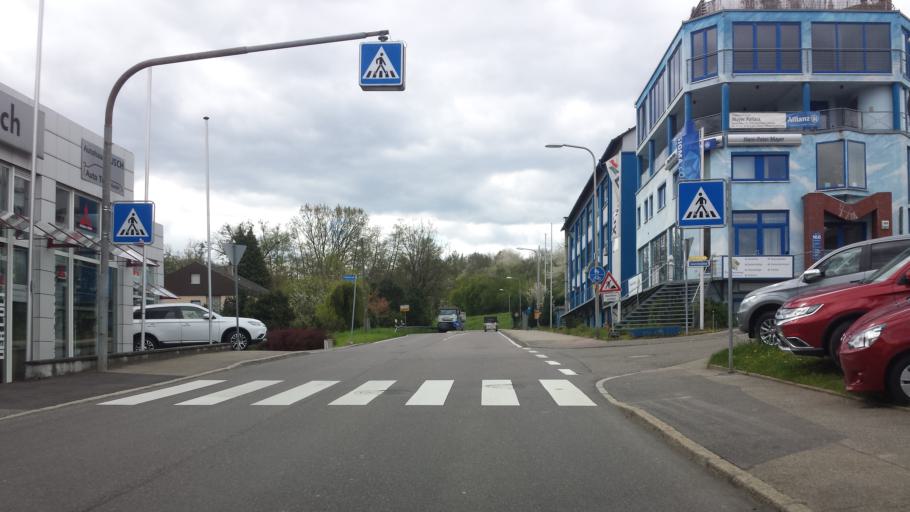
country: DE
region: Baden-Wuerttemberg
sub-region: Karlsruhe Region
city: Niefern-Oschelbronn
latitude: 48.9091
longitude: 8.7896
